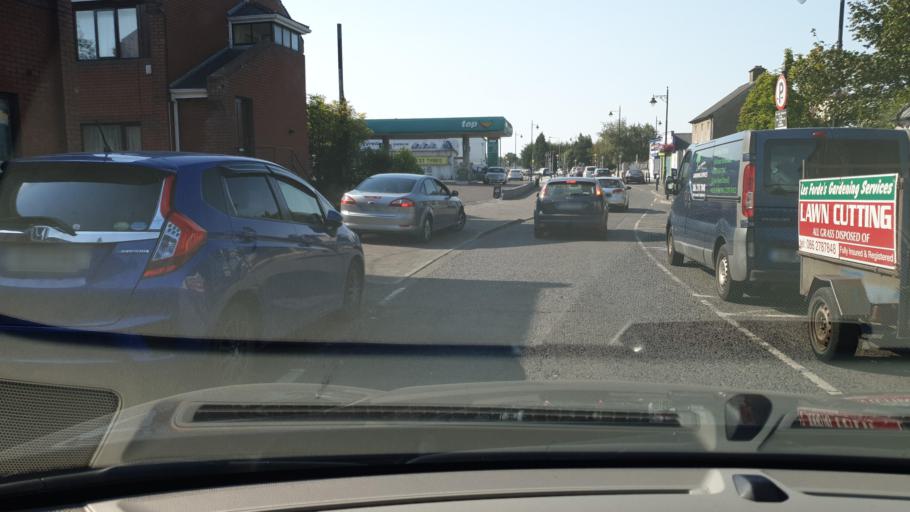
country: IE
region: Leinster
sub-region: An Mhi
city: Navan
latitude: 53.6529
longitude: -6.6901
